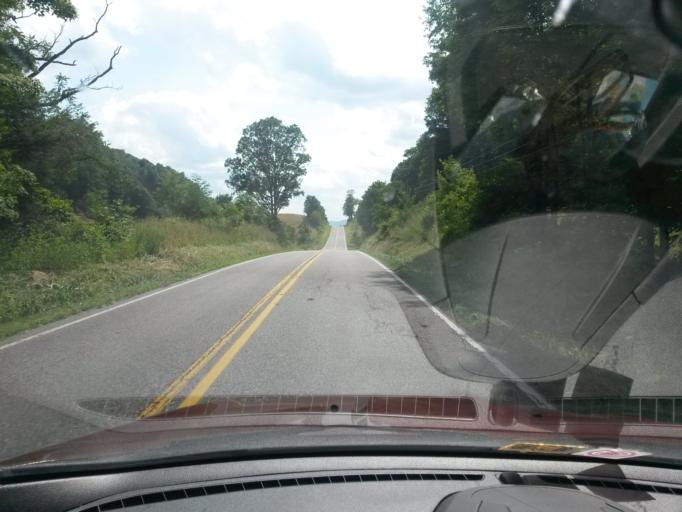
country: US
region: Virginia
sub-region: Highland County
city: Monterey
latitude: 38.4368
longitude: -79.5474
